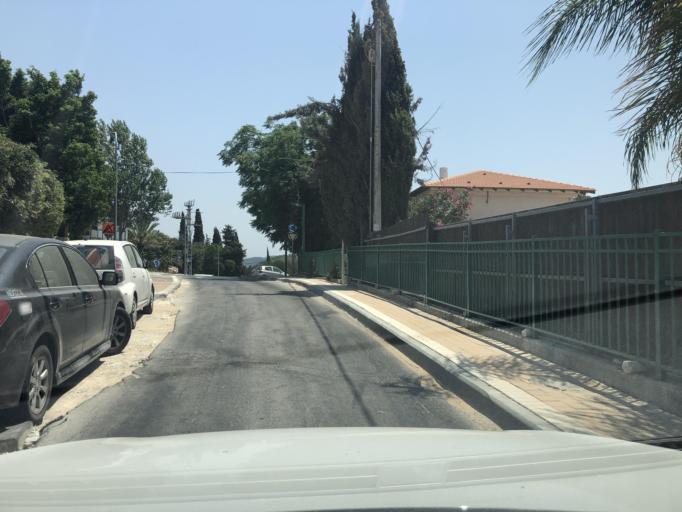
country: IL
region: Haifa
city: Daliyat el Karmil
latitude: 32.6601
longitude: 35.1083
